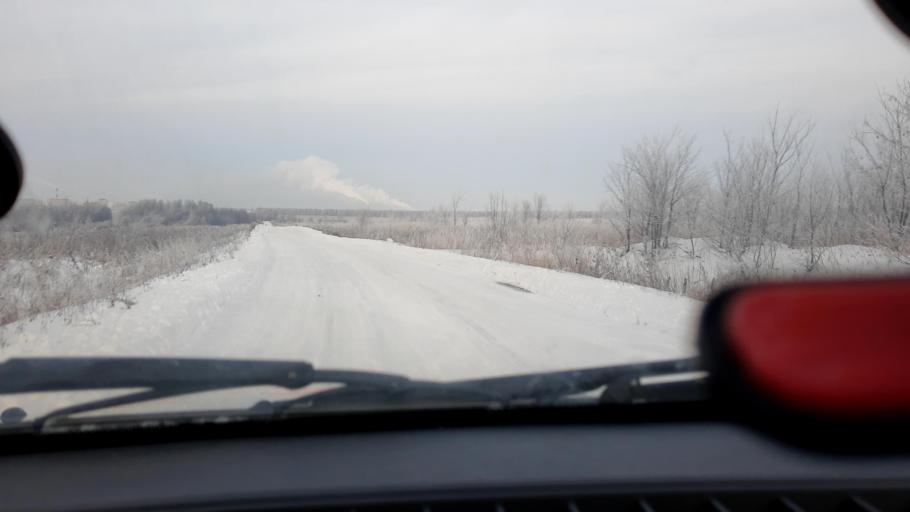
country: RU
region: Bashkortostan
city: Iglino
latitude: 54.7326
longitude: 56.2389
